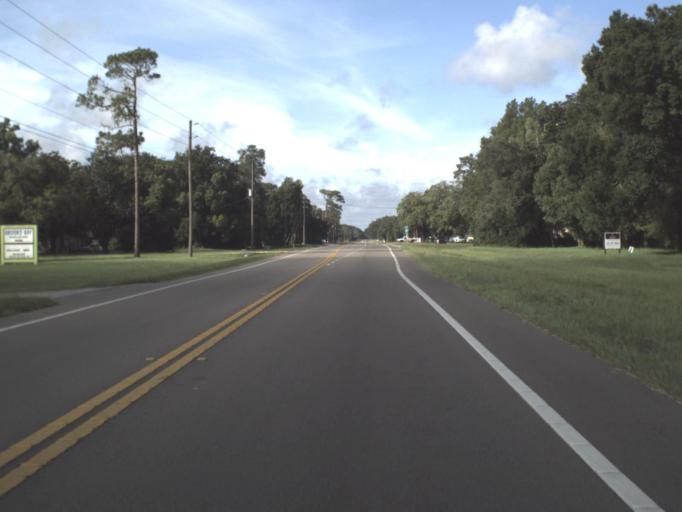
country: US
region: Florida
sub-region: Hernando County
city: Masaryktown
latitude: 28.4213
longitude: -82.4688
